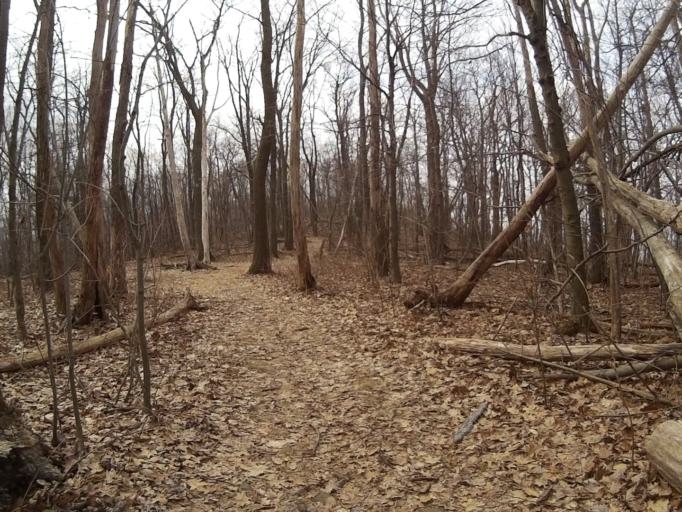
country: US
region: Pennsylvania
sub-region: Centre County
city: Lemont
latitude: 40.8131
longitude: -77.7964
